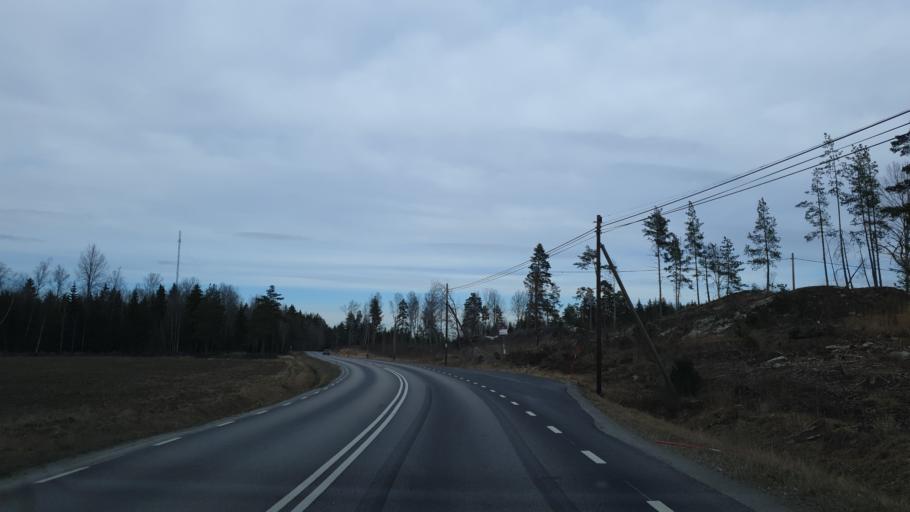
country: SE
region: Stockholm
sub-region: Osterakers Kommun
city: Akersberga
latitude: 59.5843
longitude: 18.2932
